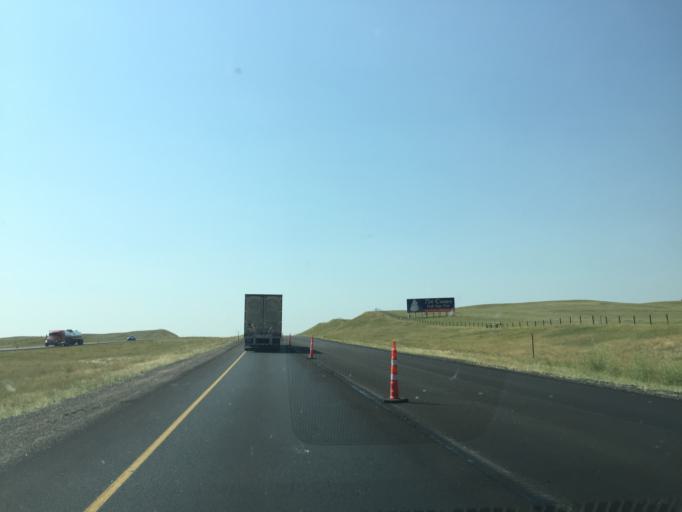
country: US
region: Wyoming
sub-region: Laramie County
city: Ranchettes
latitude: 41.3219
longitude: -104.8613
